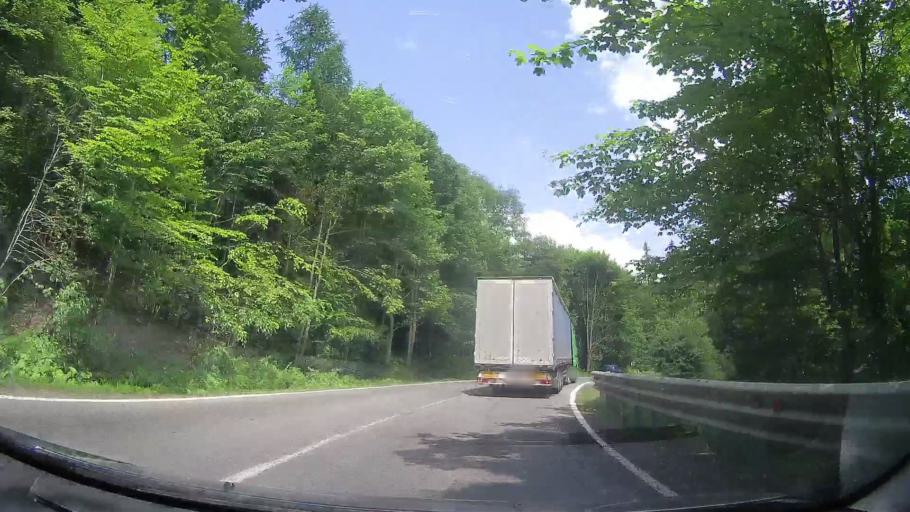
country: RO
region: Prahova
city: Maneciu
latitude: 45.3551
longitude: 25.9424
